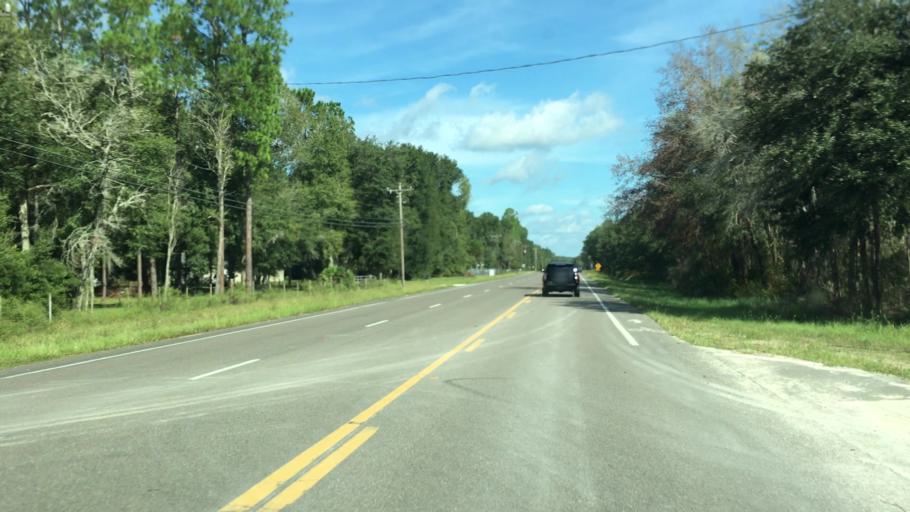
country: US
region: Florida
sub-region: Alachua County
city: Gainesville
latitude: 29.7212
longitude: -82.2771
